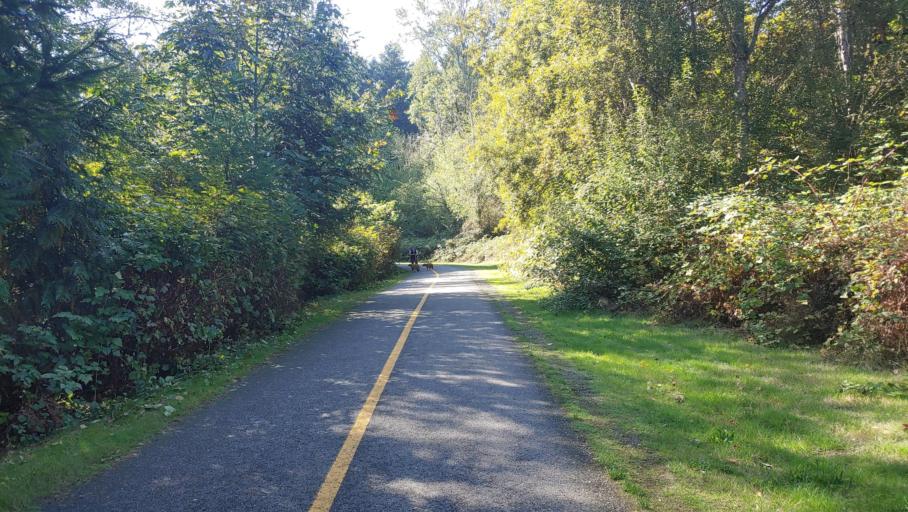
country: US
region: Washington
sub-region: King County
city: Des Moines
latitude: 47.4213
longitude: -122.3059
